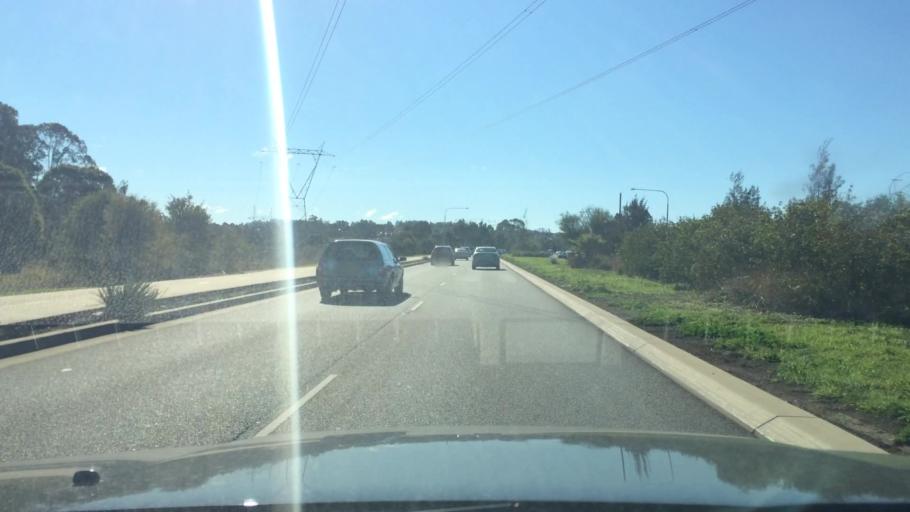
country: AU
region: New South Wales
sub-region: Fairfield
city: Cecil Park
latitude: -33.9038
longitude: 150.8551
